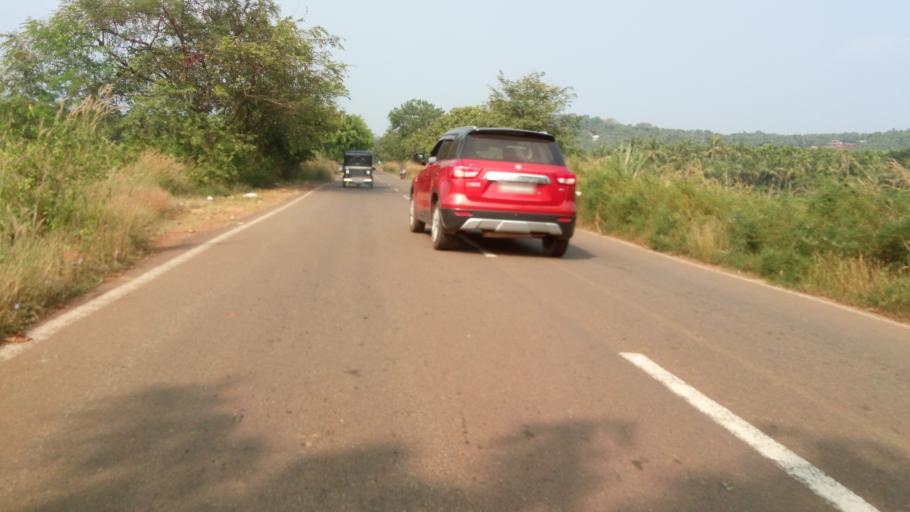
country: IN
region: Kerala
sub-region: Malappuram
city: Malappuram
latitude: 10.9960
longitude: 76.0144
